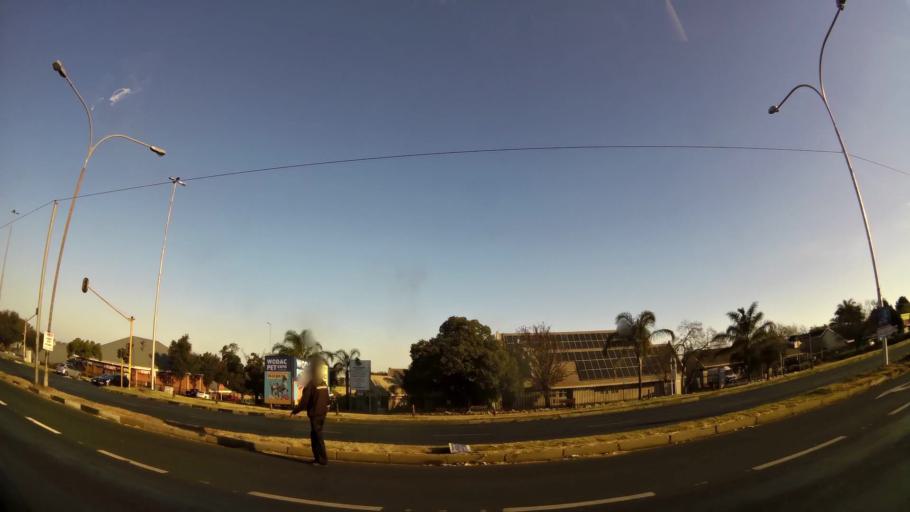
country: ZA
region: Gauteng
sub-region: City of Johannesburg Metropolitan Municipality
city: Roodepoort
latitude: -26.1472
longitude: 27.9008
